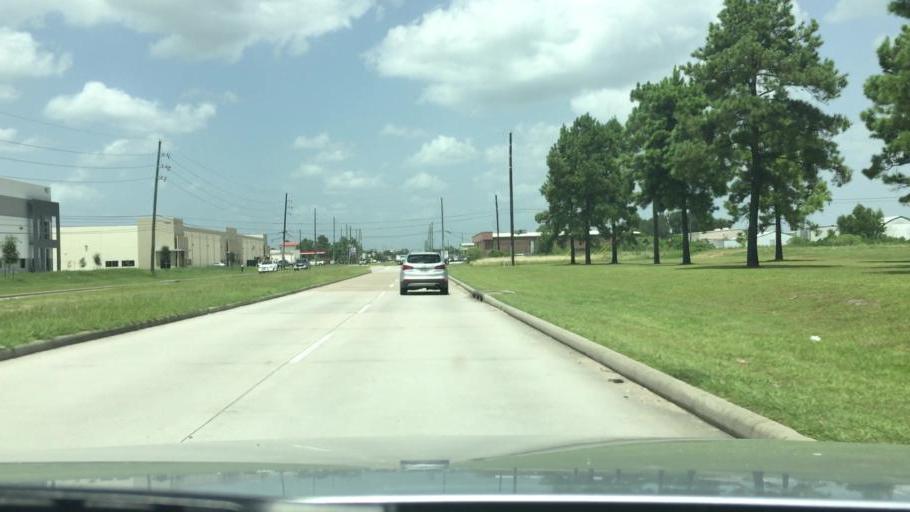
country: US
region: Texas
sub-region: Harris County
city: Hudson
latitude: 29.9529
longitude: -95.5223
